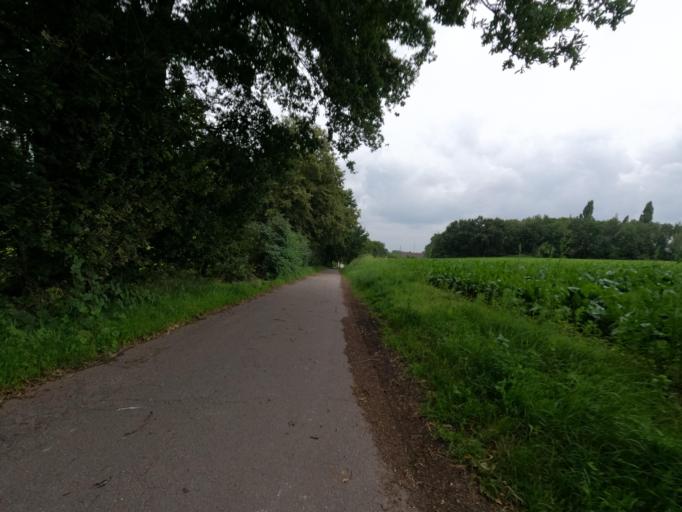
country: DE
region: North Rhine-Westphalia
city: Geilenkirchen
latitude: 50.9733
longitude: 6.1517
